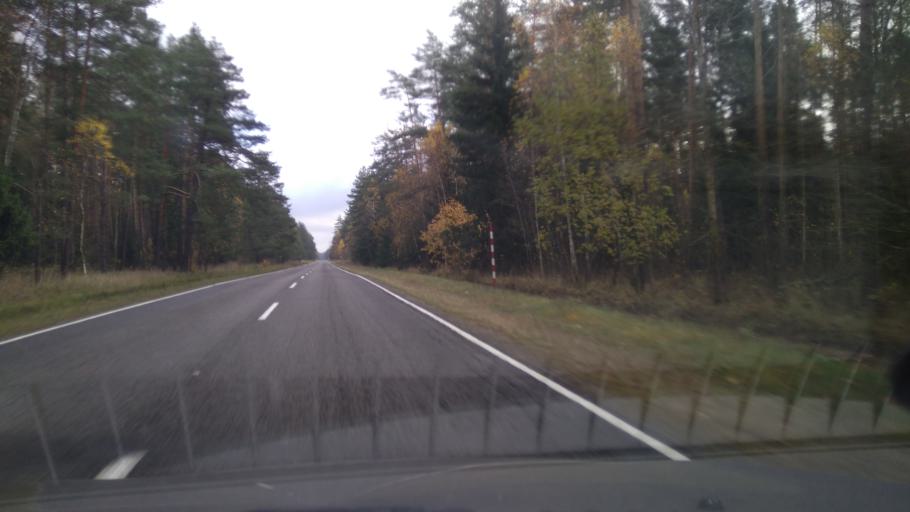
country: BY
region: Minsk
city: Slutsk
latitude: 53.2299
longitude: 27.6952
